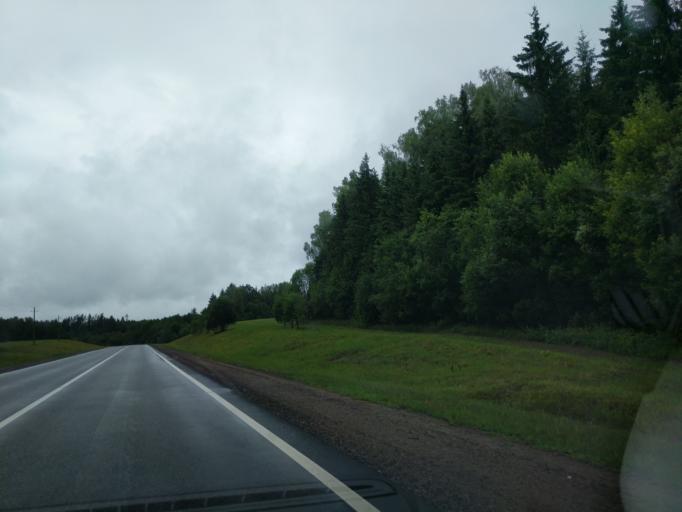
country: BY
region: Minsk
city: Syomkava
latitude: 54.2206
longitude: 27.4942
